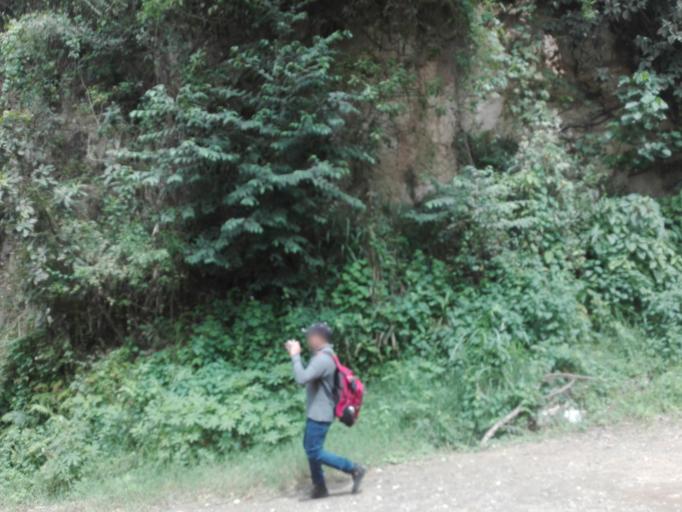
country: GT
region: Guatemala
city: Petapa
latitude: 14.5142
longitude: -90.5202
